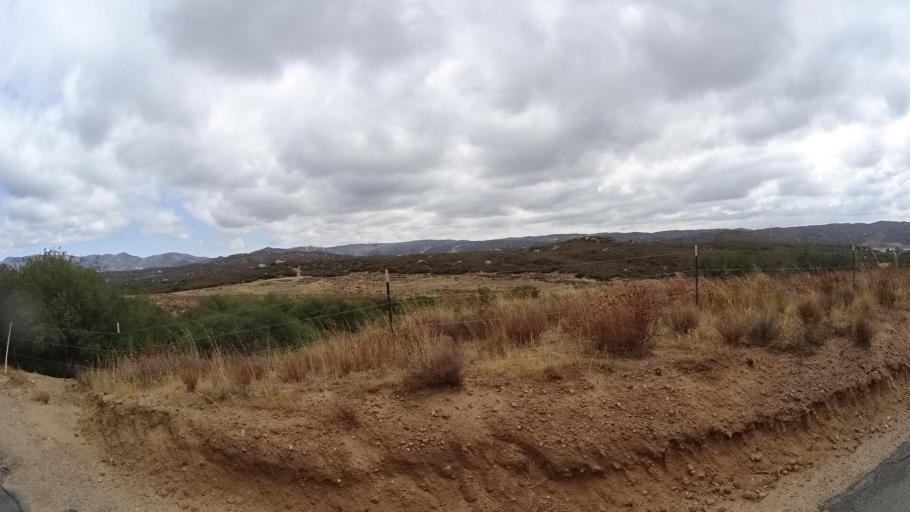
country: US
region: California
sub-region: San Diego County
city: Pine Valley
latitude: 32.7356
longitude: -116.4540
